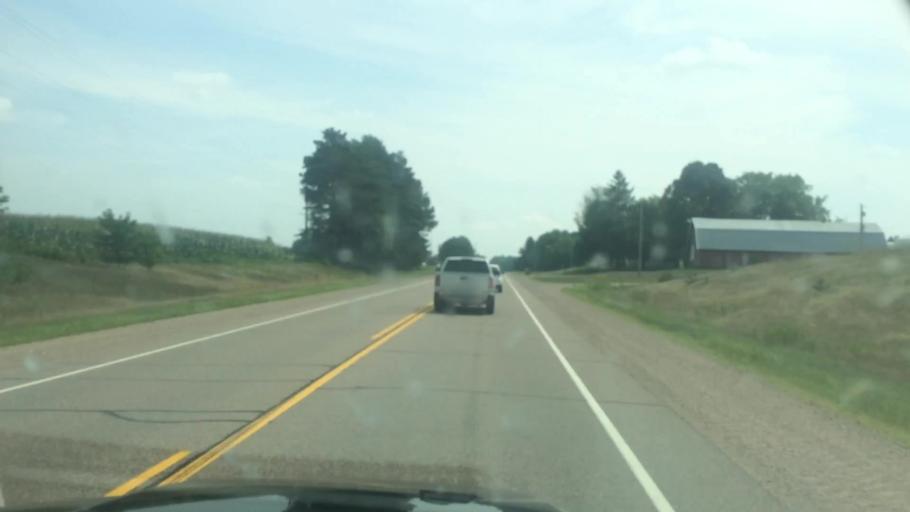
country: US
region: Wisconsin
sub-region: Langlade County
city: Antigo
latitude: 45.1613
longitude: -89.0348
